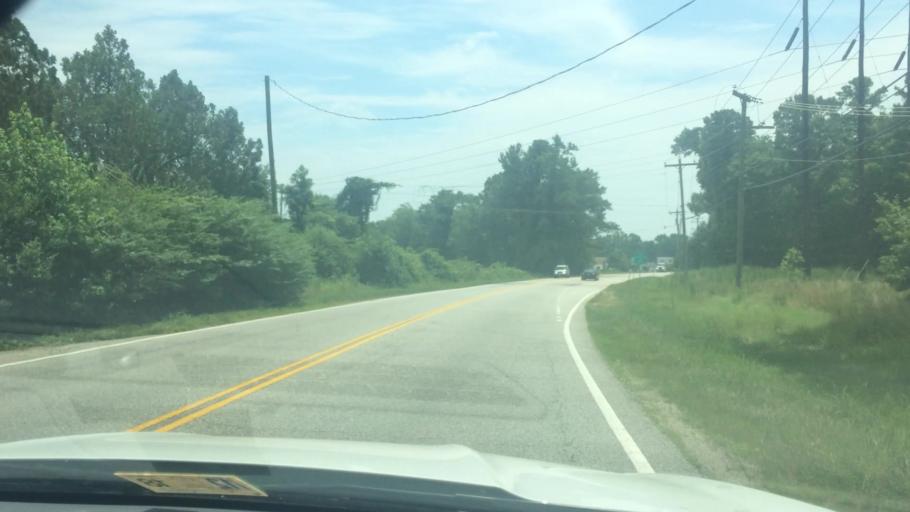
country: US
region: Virginia
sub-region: City of Williamsburg
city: Williamsburg
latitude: 37.2329
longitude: -76.6281
